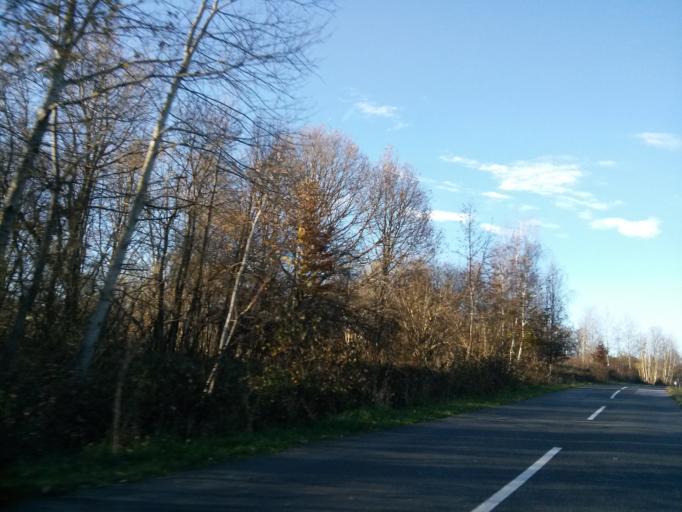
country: HR
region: Sisacko-Moslavacka
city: Gvozd
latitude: 45.3878
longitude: 15.9150
